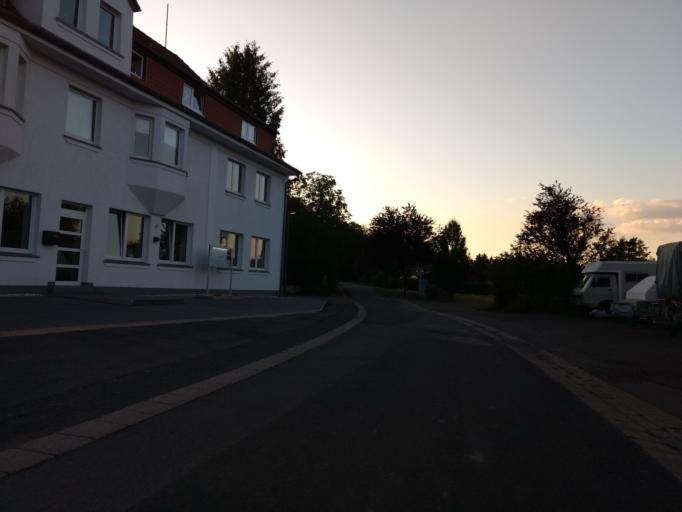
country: DE
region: Saarland
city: Nalbach
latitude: 49.4056
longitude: 6.7813
